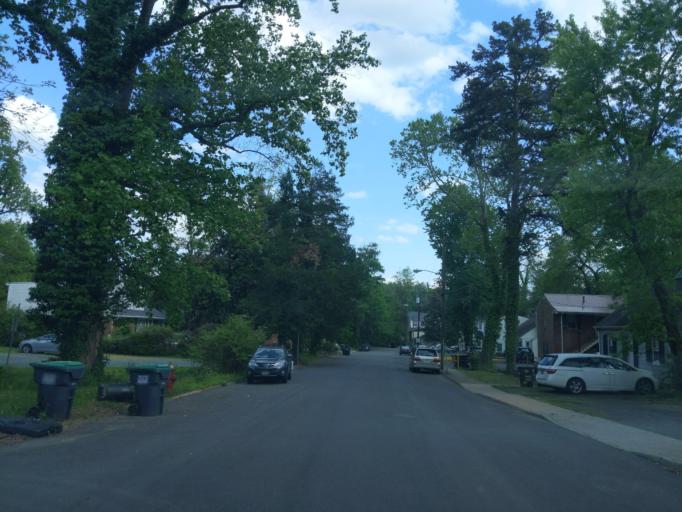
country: US
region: Virginia
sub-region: City of Charlottesville
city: Charlottesville
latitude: 38.0286
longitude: -78.5134
